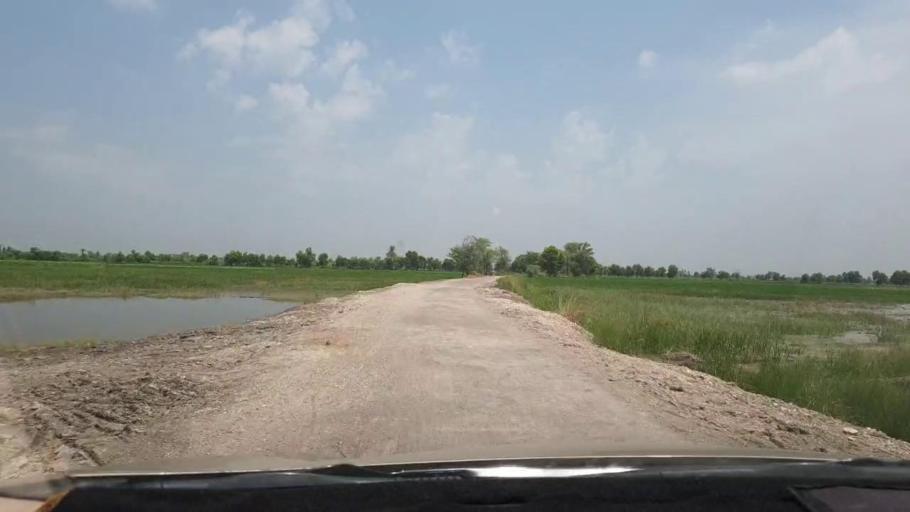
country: PK
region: Sindh
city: Naudero
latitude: 27.7345
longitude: 68.3428
